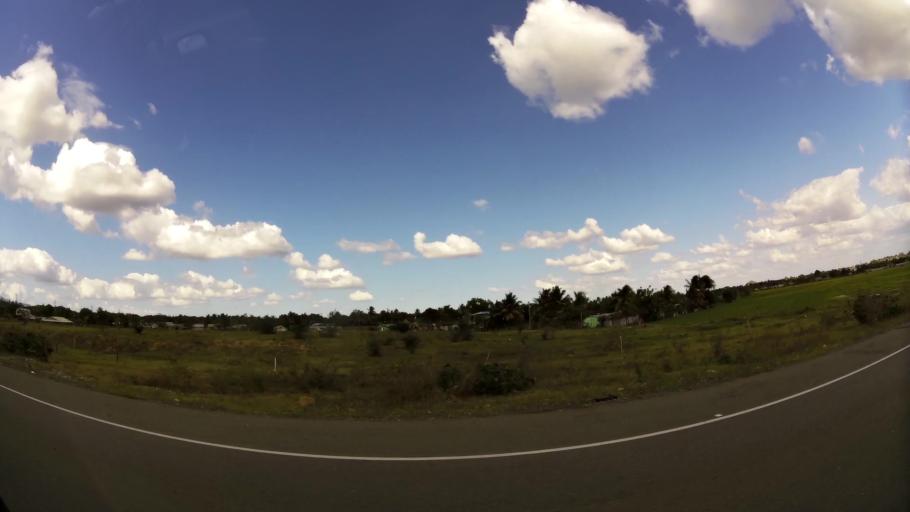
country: DO
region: Santo Domingo
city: Santo Domingo Oeste
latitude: 18.5361
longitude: -70.0747
